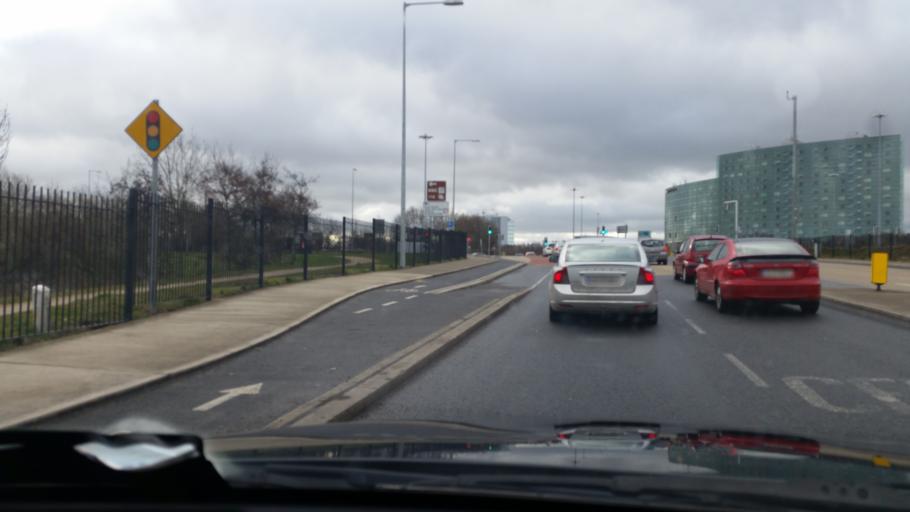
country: IE
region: Leinster
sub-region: Fingal County
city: Blanchardstown
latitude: 53.3988
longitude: -6.3914
